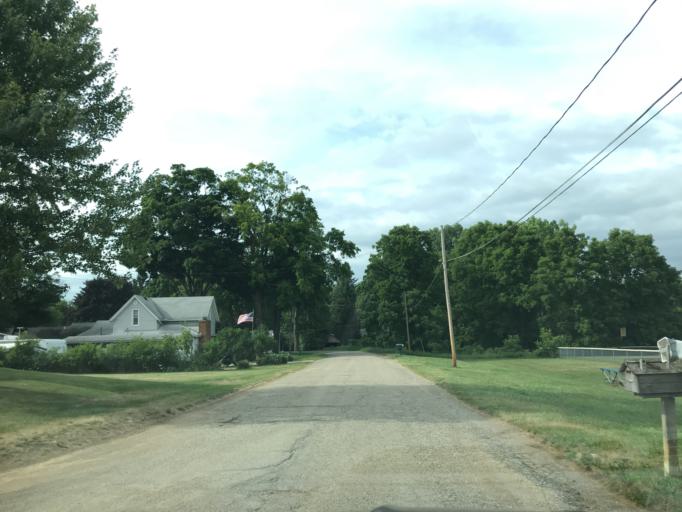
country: US
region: Michigan
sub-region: Jackson County
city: Spring Arbor
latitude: 42.1472
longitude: -84.5164
